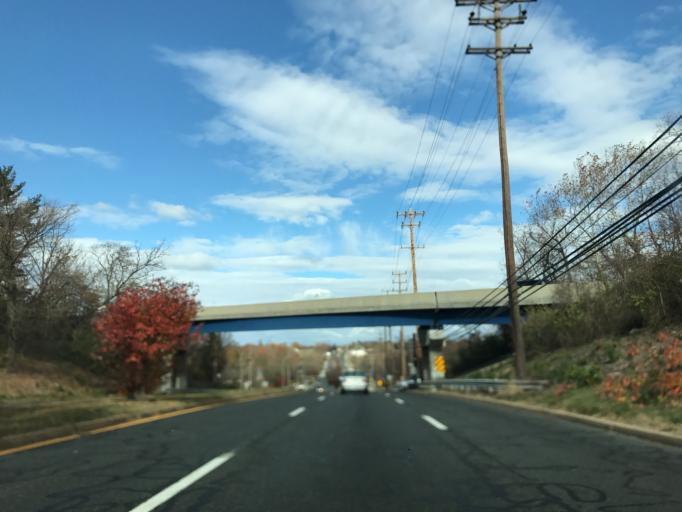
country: US
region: Maryland
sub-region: Anne Arundel County
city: Brooklyn Park
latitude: 39.2014
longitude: -76.6136
